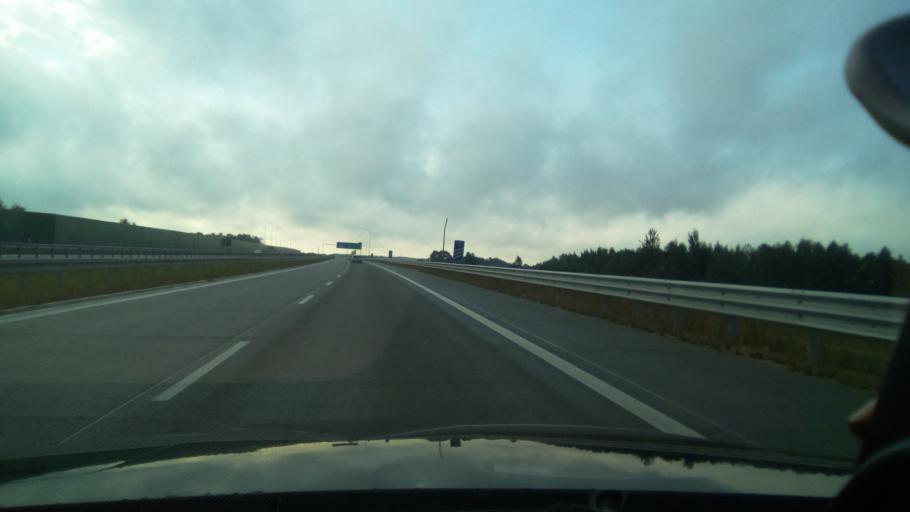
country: PL
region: Silesian Voivodeship
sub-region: Powiat czestochowski
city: Konopiska
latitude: 50.7492
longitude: 19.0353
